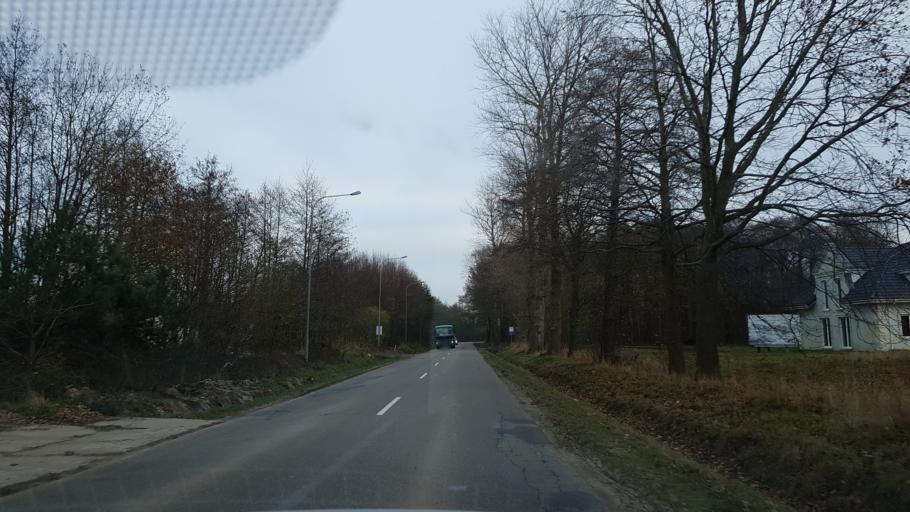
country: PL
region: West Pomeranian Voivodeship
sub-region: Powiat kolobrzeski
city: Grzybowo
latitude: 54.1612
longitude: 15.5113
